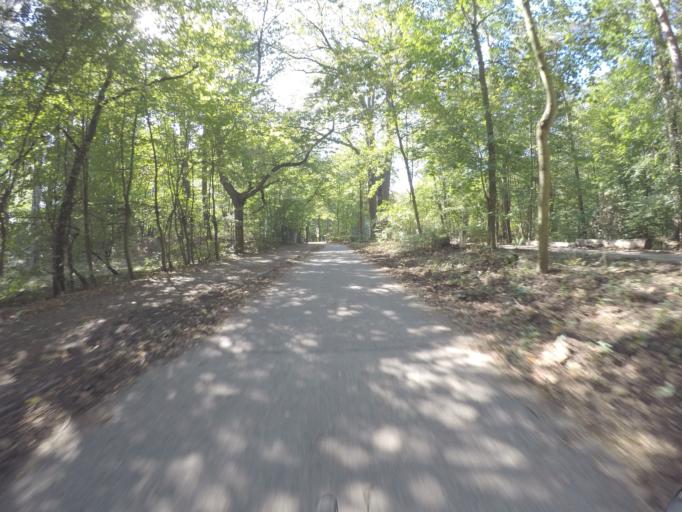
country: DE
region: Berlin
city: Konradshohe
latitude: 52.5795
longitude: 13.2446
